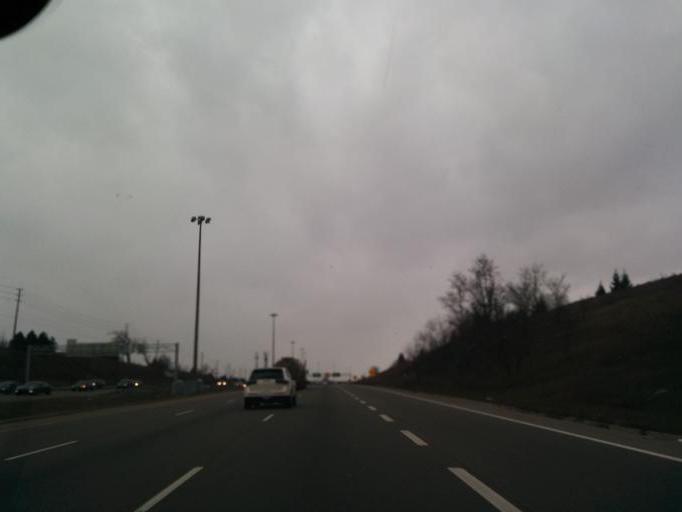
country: CA
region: Ontario
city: Brampton
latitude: 43.7201
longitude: -79.7578
